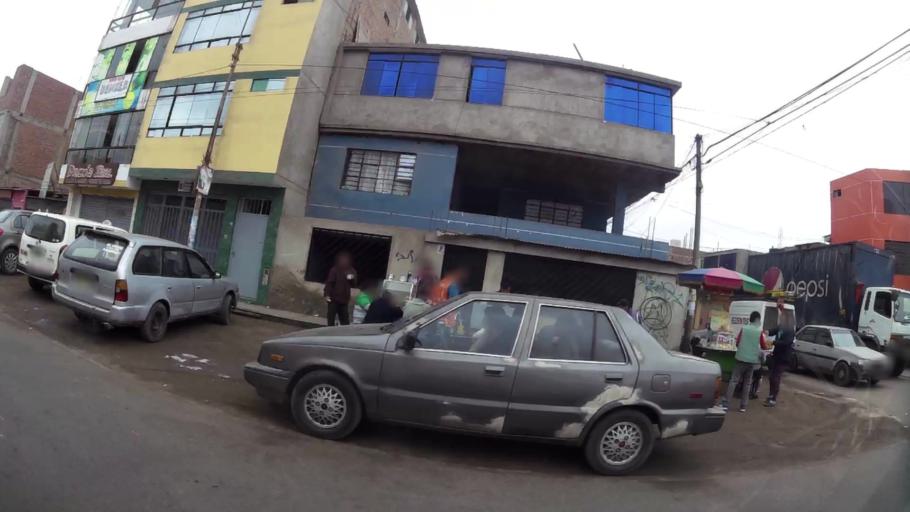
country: PE
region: Lima
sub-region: Lima
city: Surco
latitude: -12.1931
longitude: -76.9814
